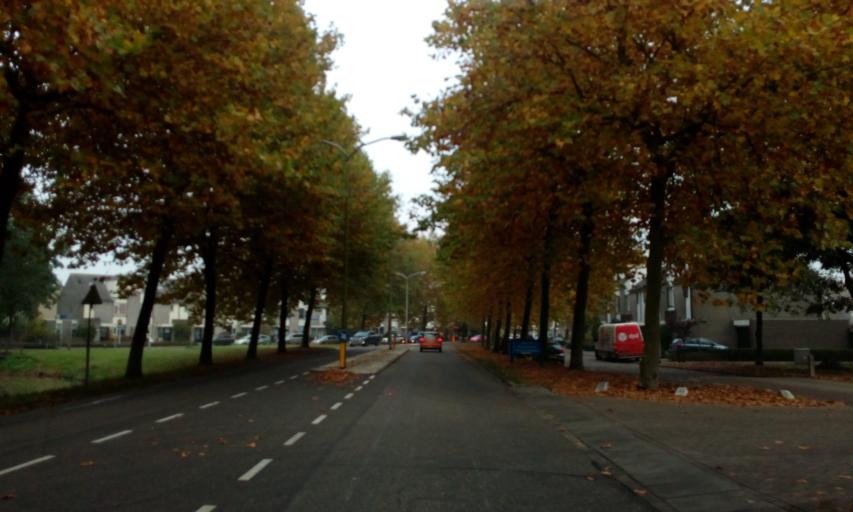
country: NL
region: South Holland
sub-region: Gemeente Waddinxveen
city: Groenswaard
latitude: 52.0376
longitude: 4.6352
